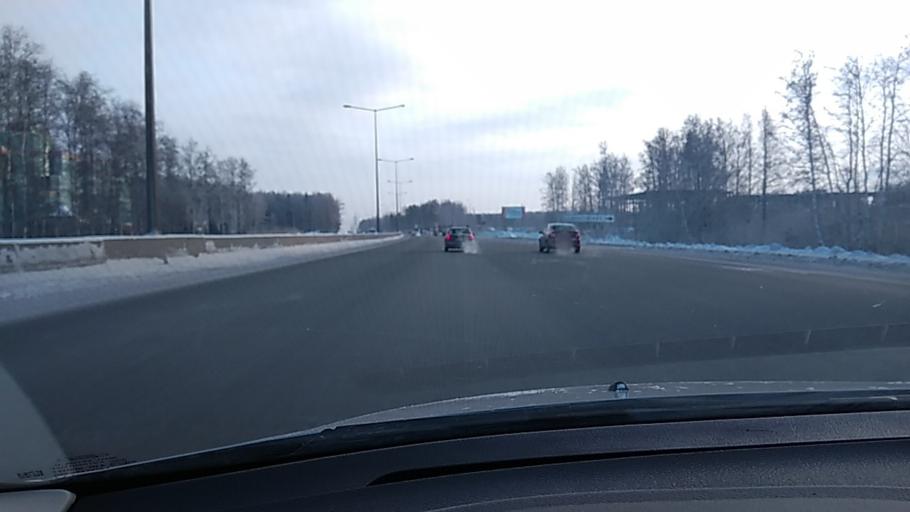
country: RU
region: Sverdlovsk
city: Istok
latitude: 56.7760
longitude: 60.7140
